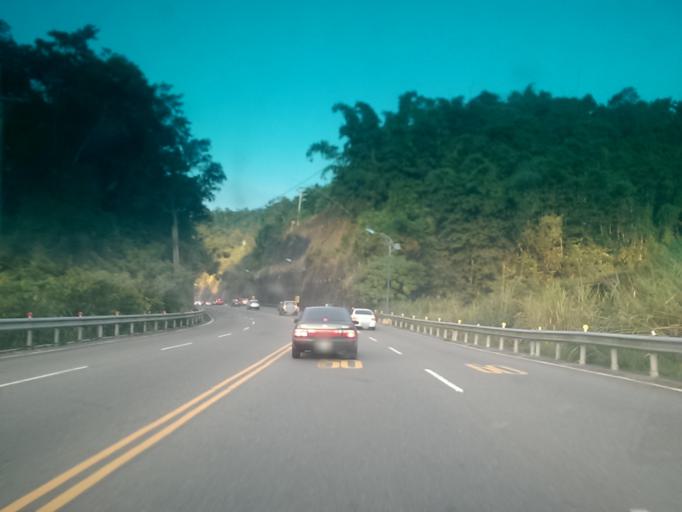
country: TW
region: Taiwan
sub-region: Nantou
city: Puli
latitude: 23.9333
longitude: 120.9241
